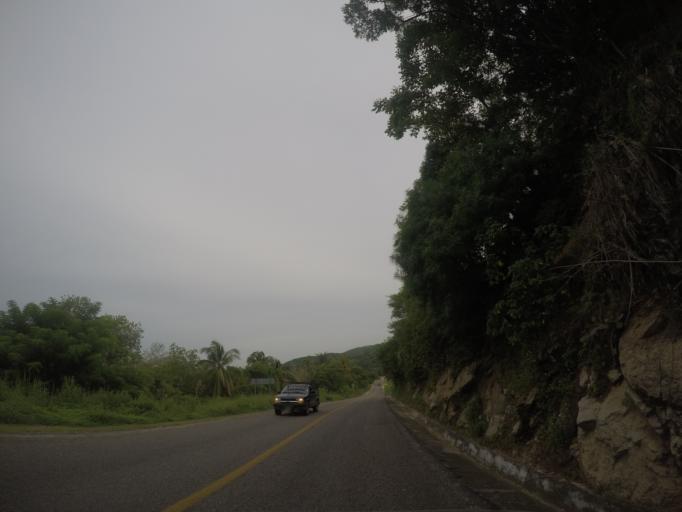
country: MX
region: Oaxaca
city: San Pedro Mixtepec
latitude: 15.9372
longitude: -97.1576
